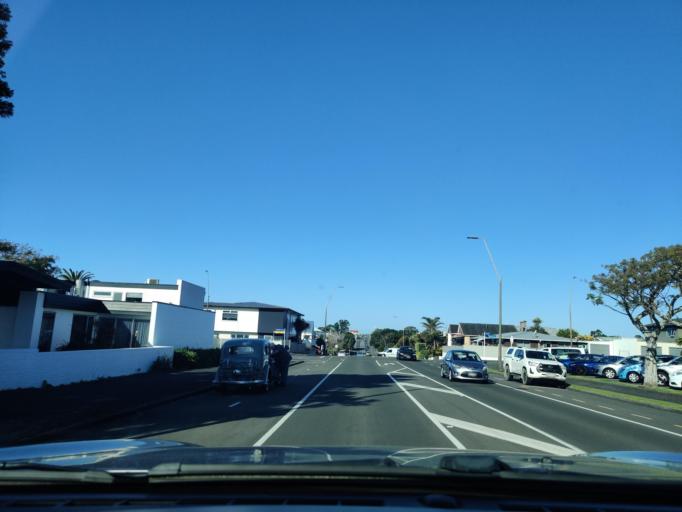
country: NZ
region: Taranaki
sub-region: New Plymouth District
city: New Plymouth
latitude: -39.0532
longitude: 174.0891
